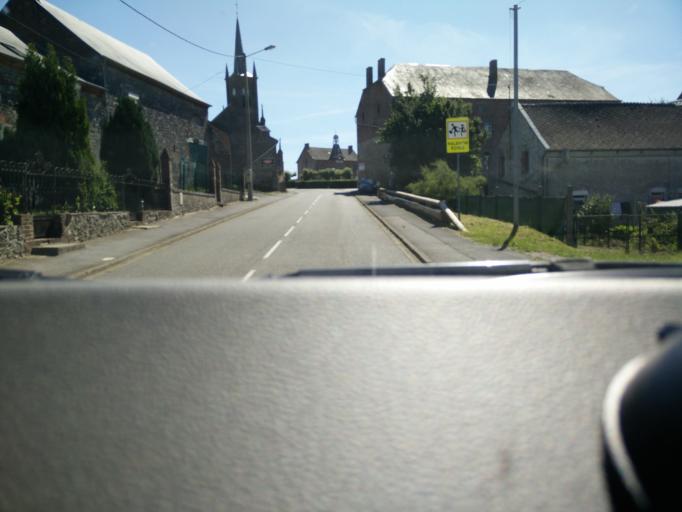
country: FR
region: Nord-Pas-de-Calais
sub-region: Departement du Nord
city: Avesnelles
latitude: 50.1763
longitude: 3.9362
